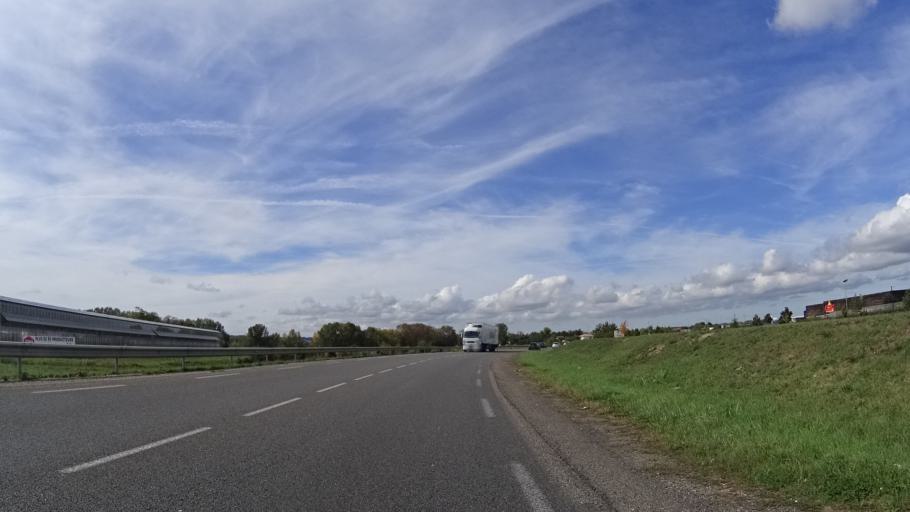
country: FR
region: Aquitaine
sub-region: Departement du Lot-et-Garonne
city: Boe
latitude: 44.1735
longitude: 0.6314
